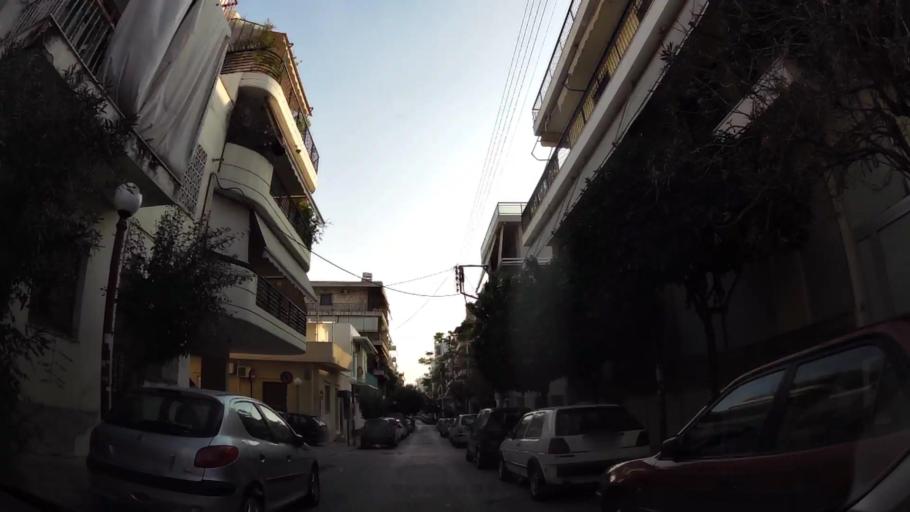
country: GR
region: Attica
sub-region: Nomarchia Athinas
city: Dhafni
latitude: 37.9516
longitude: 23.7330
